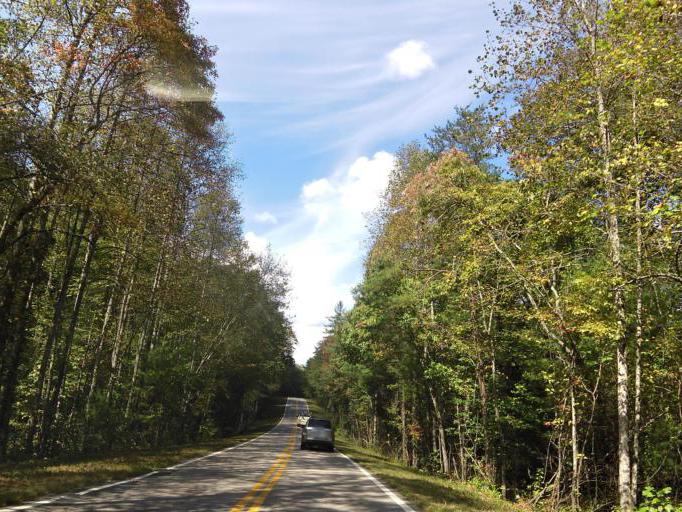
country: US
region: Georgia
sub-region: Pickens County
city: Nelson
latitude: 34.4948
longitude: -84.2663
